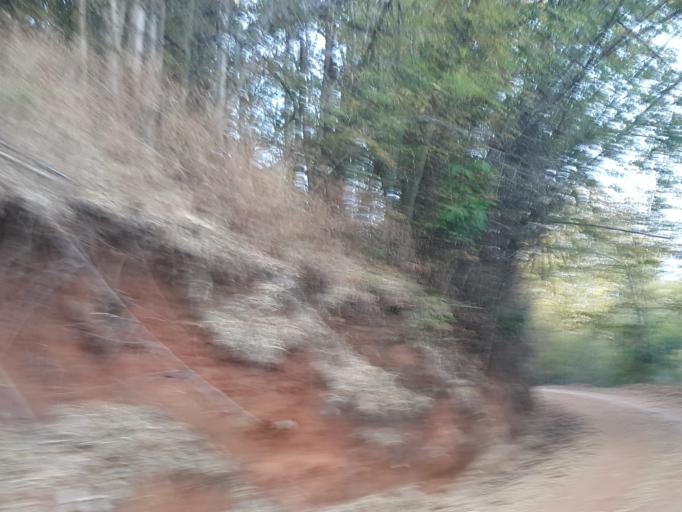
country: TH
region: Chiang Mai
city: Mae Taeng
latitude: 19.0586
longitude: 98.7691
